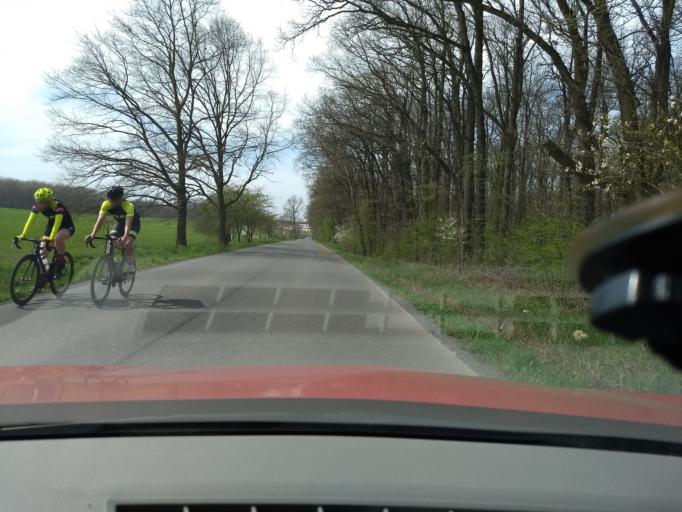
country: CZ
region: Central Bohemia
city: Hostivice
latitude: 50.0678
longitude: 14.2578
